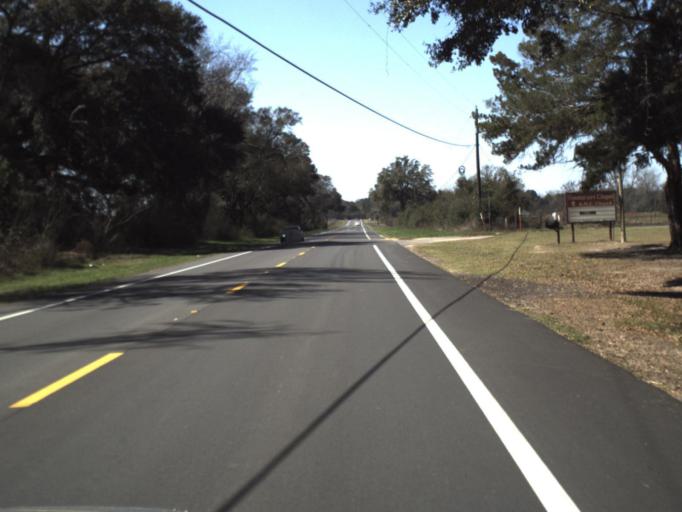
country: US
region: Florida
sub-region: Jackson County
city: Malone
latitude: 30.8700
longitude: -85.1399
